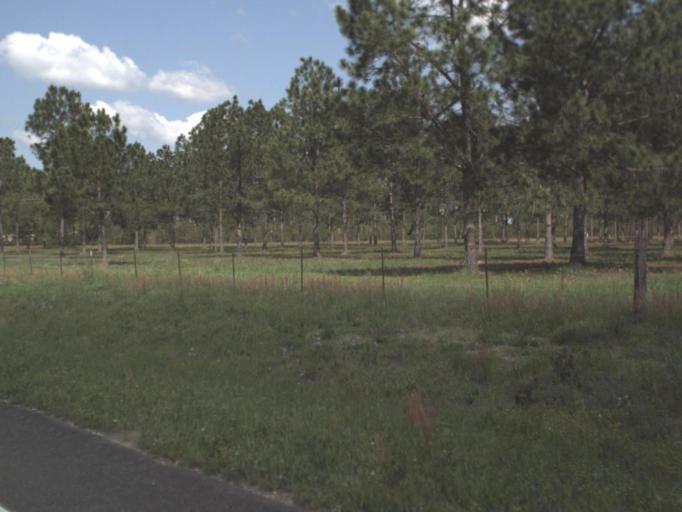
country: US
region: Florida
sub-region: Santa Rosa County
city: Point Baker
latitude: 30.8575
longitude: -86.8703
